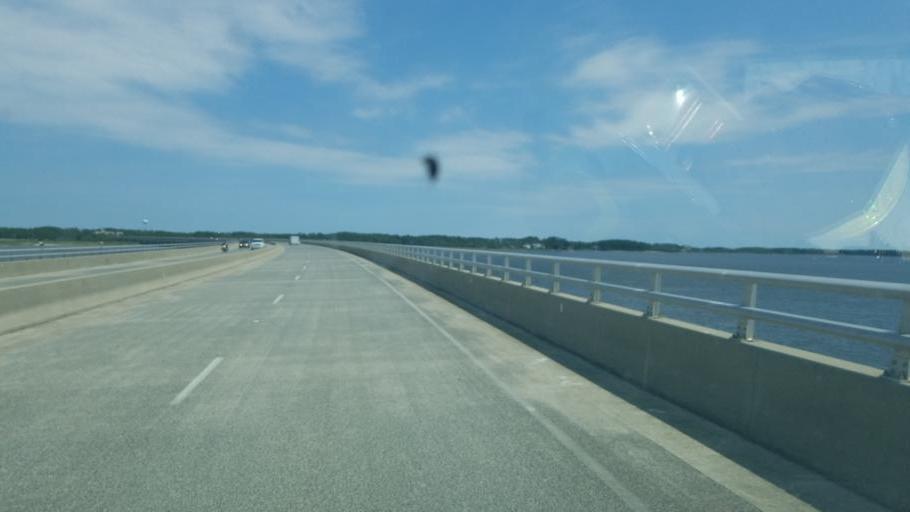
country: US
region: North Carolina
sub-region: Dare County
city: Manteo
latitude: 35.8817
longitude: -75.6836
